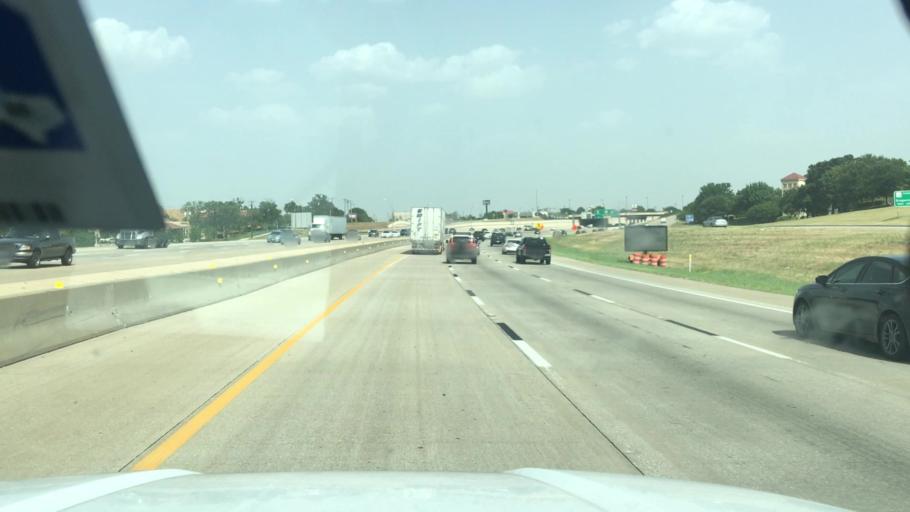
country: US
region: Texas
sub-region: Tarrant County
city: Southlake
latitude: 32.9428
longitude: -97.1071
